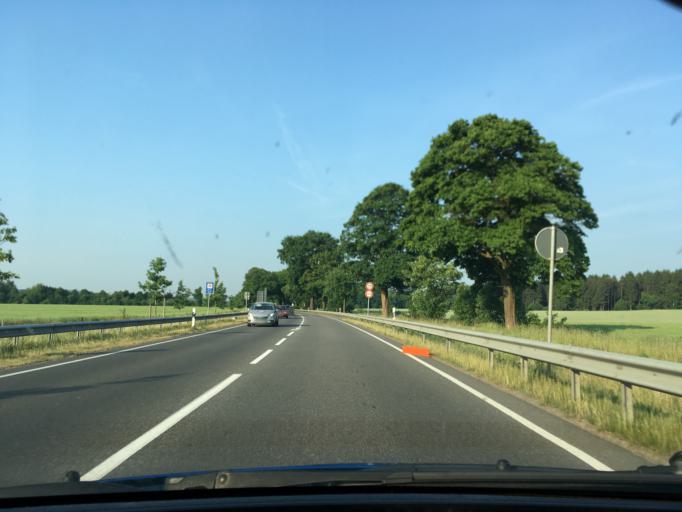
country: DE
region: Lower Saxony
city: Buchholz in der Nordheide
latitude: 53.3594
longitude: 9.8678
